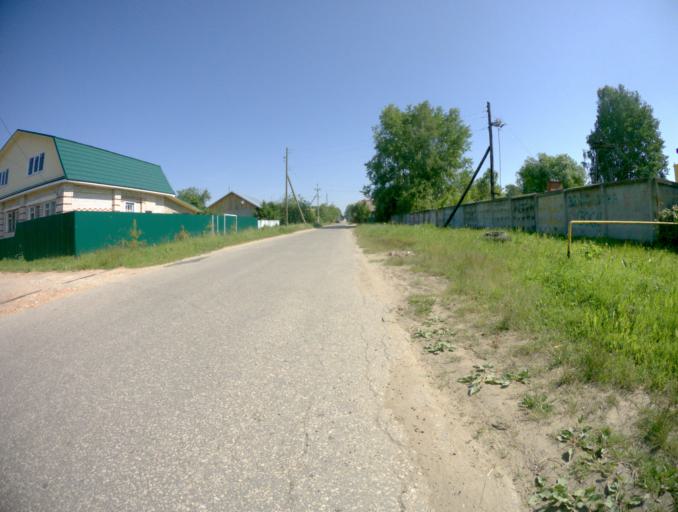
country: RU
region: Vladimir
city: Vyazniki
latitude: 56.2332
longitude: 42.1946
